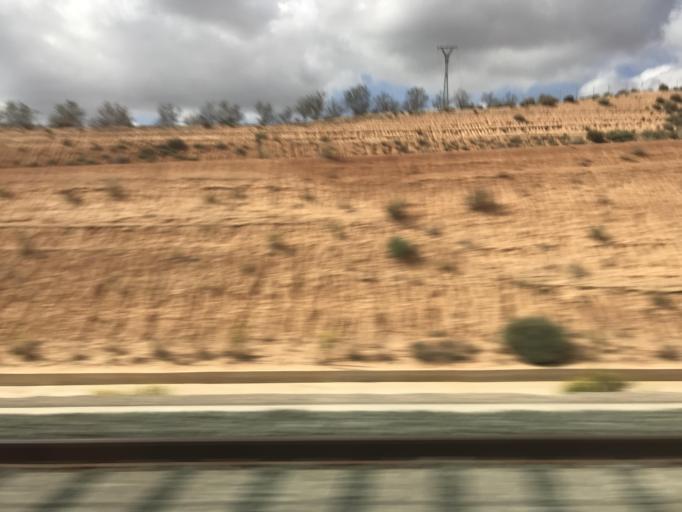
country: ES
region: Castille-La Mancha
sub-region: Provincia de Albacete
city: Caudete
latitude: 38.7333
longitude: -0.9374
